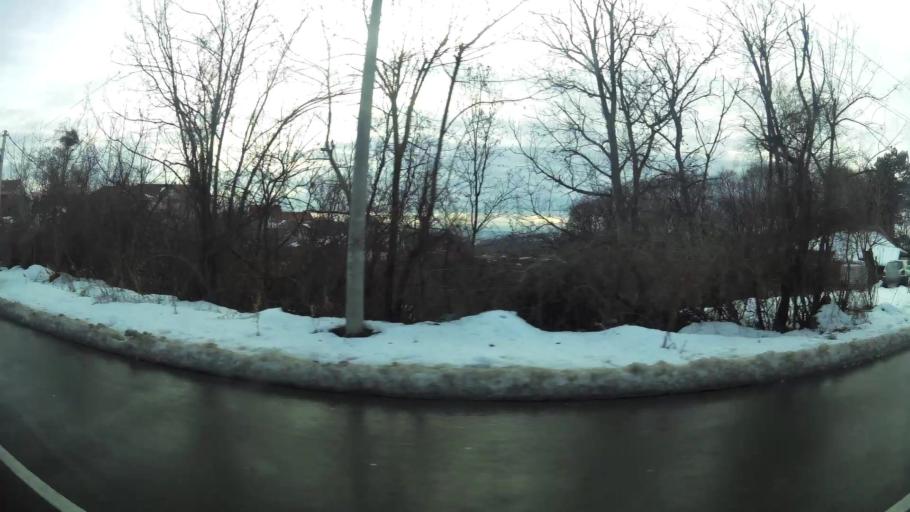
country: RS
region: Central Serbia
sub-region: Belgrade
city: Zvezdara
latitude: 44.7387
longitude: 20.5131
